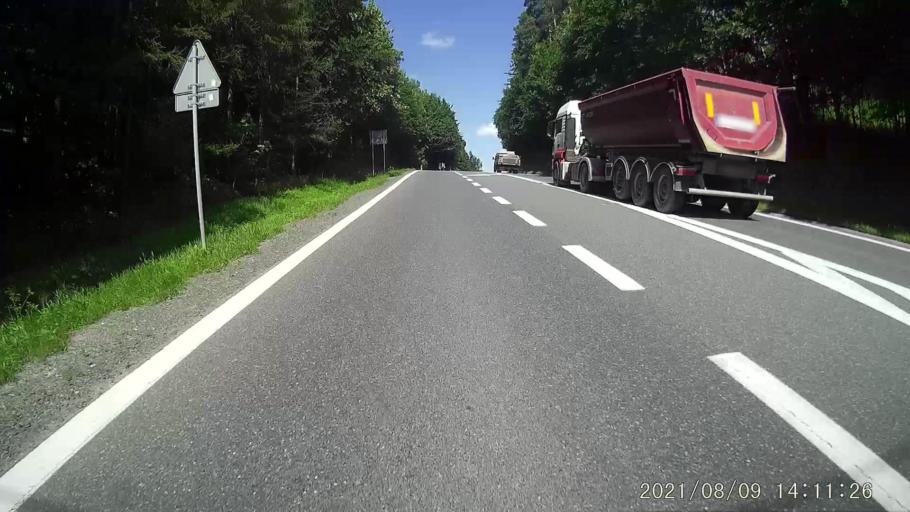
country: PL
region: Lower Silesian Voivodeship
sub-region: Powiat zabkowicki
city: Bardo
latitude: 50.4891
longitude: 16.7178
